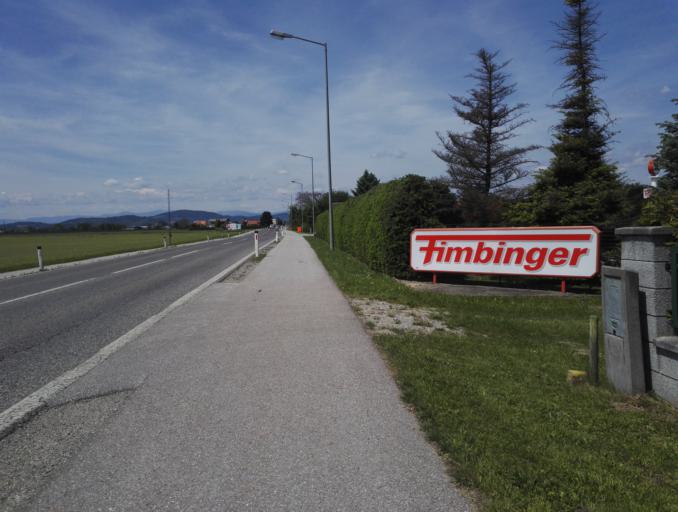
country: AT
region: Styria
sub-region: Politischer Bezirk Graz-Umgebung
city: Gossendorf
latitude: 46.9786
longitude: 15.4675
